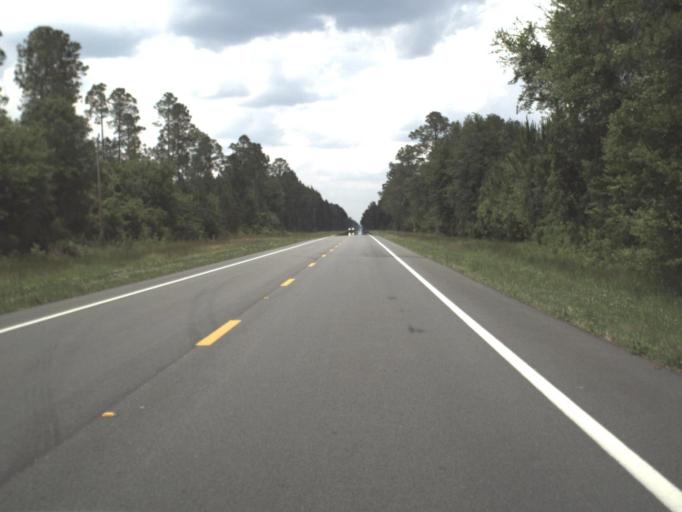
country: US
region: Florida
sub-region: Columbia County
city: Five Points
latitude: 30.3942
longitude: -82.6298
